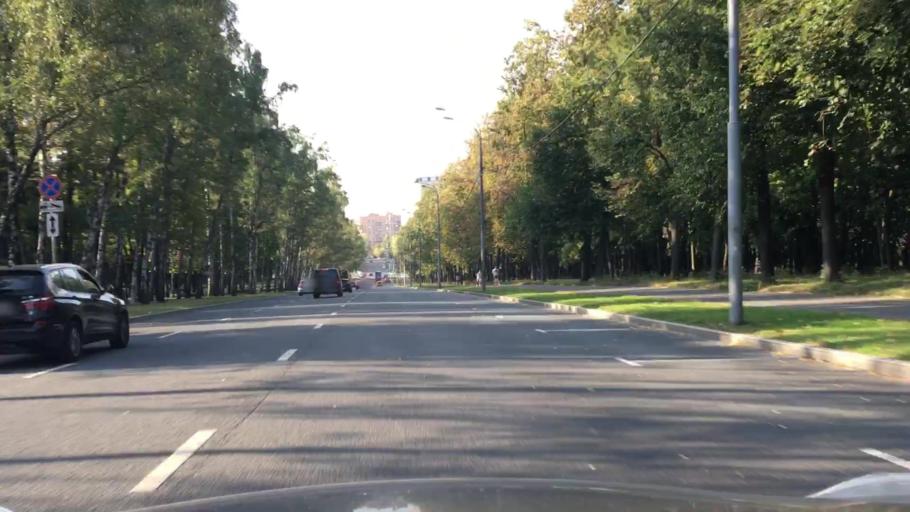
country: RU
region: Moscow
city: Vorob'yovo
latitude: 55.7091
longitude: 37.5323
